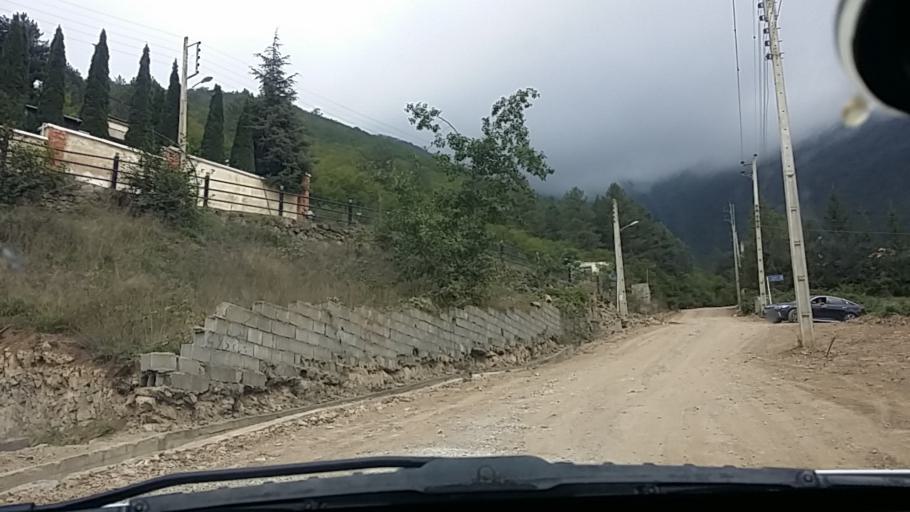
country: IR
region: Mazandaran
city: `Abbasabad
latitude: 36.4928
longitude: 51.1659
